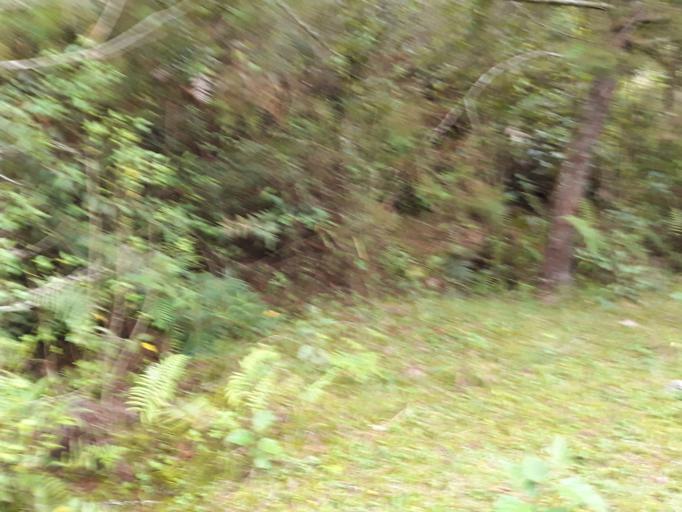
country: GT
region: Quiche
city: Nebaj
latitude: 15.4286
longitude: -91.1366
